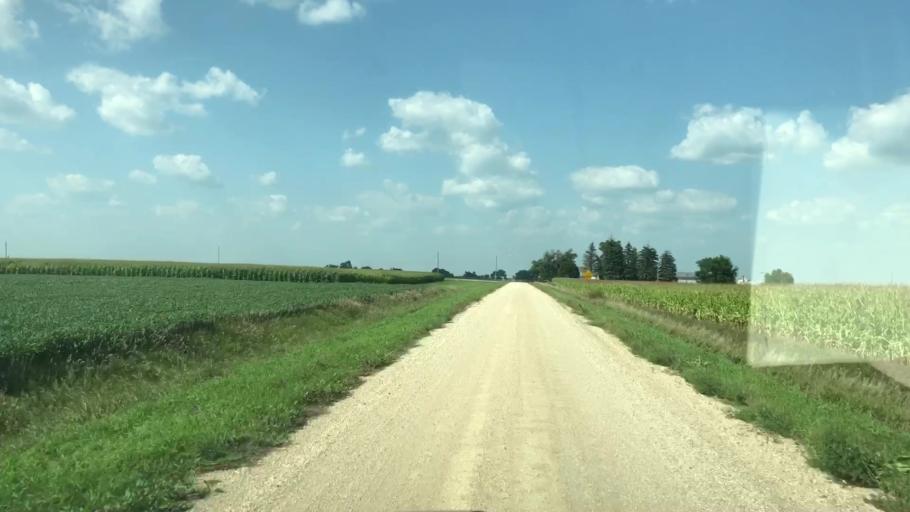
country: US
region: Iowa
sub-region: O'Brien County
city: Sheldon
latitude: 43.1833
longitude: -95.7824
